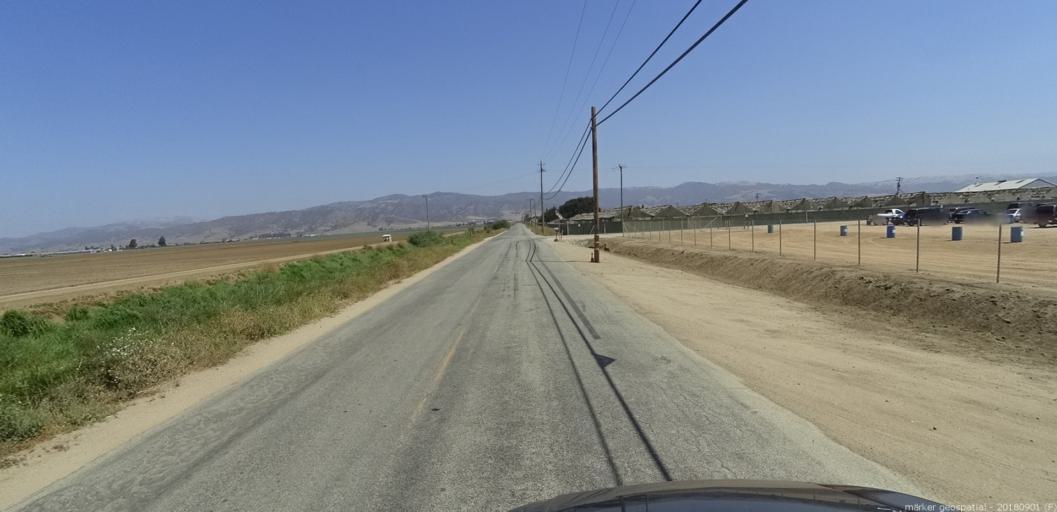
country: US
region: California
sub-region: Monterey County
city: Chualar
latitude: 36.6080
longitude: -121.5535
